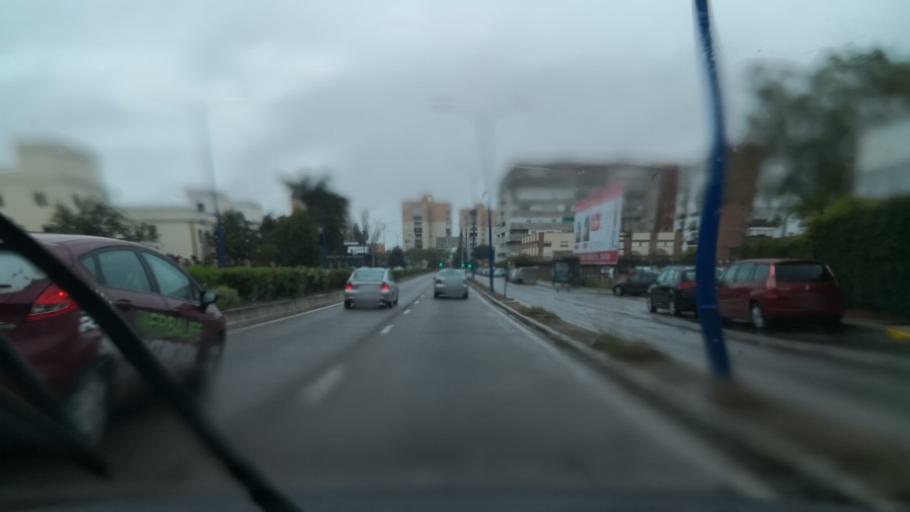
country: ES
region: Extremadura
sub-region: Provincia de Badajoz
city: Badajoz
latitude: 38.8710
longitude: -6.9788
